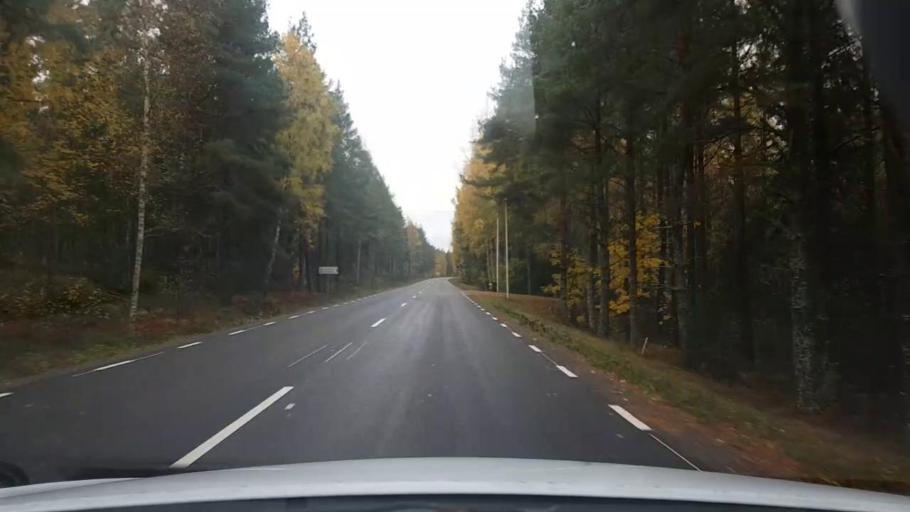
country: SE
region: OErebro
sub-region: Laxa Kommun
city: Laxa
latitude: 58.7988
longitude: 14.5423
